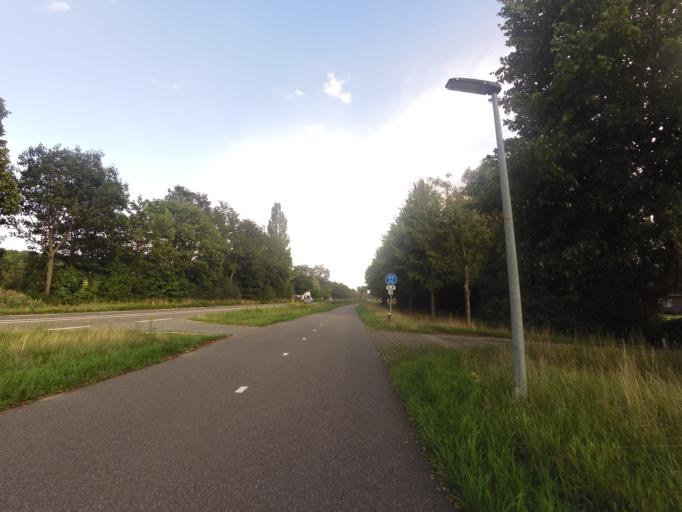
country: NL
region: Gelderland
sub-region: Gemeente Doetinchem
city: Doetinchem
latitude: 51.9412
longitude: 6.3163
